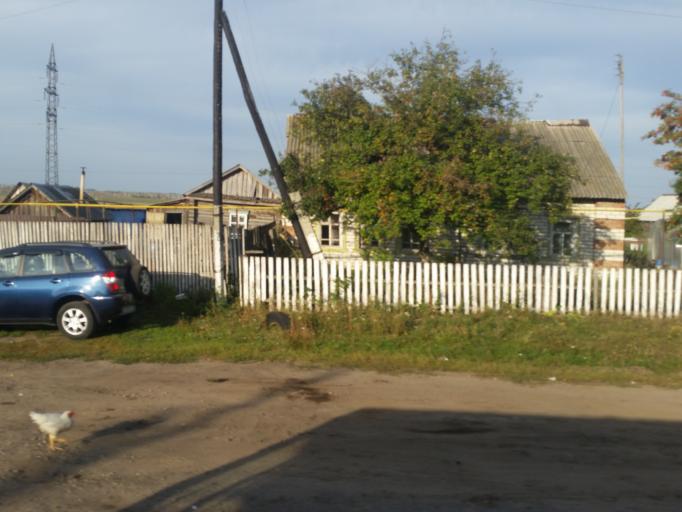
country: RU
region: Ulyanovsk
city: Mullovka
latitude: 54.2669
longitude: 49.1672
